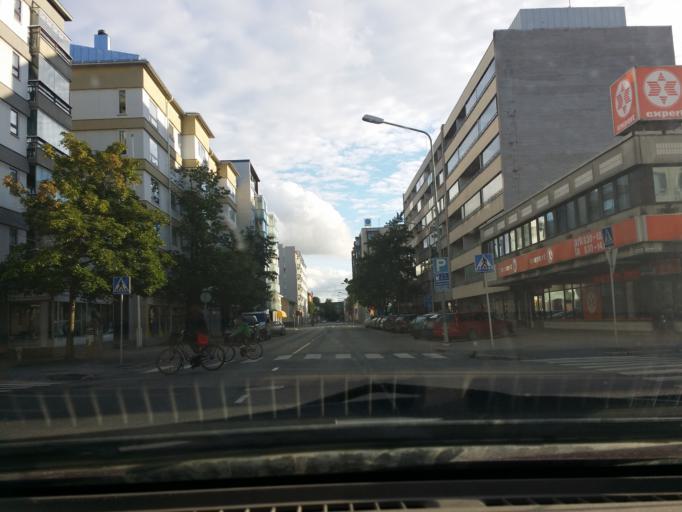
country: FI
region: Satakunta
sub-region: Pori
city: Pori
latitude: 61.4843
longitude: 21.7946
